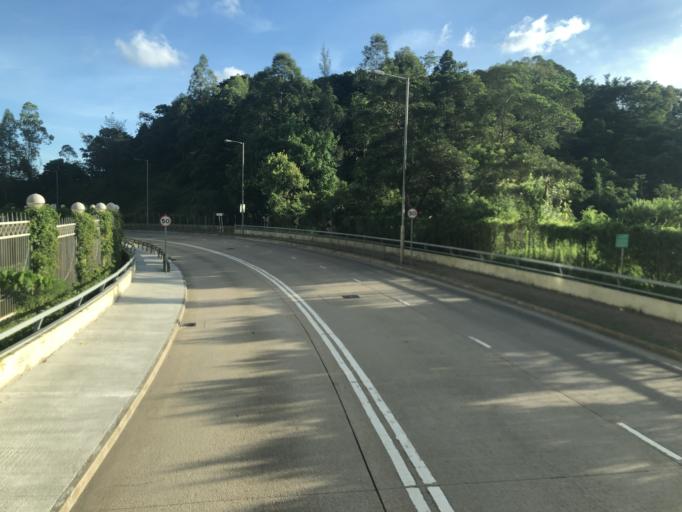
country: HK
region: Kowloon City
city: Kowloon
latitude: 22.3325
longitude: 114.2210
